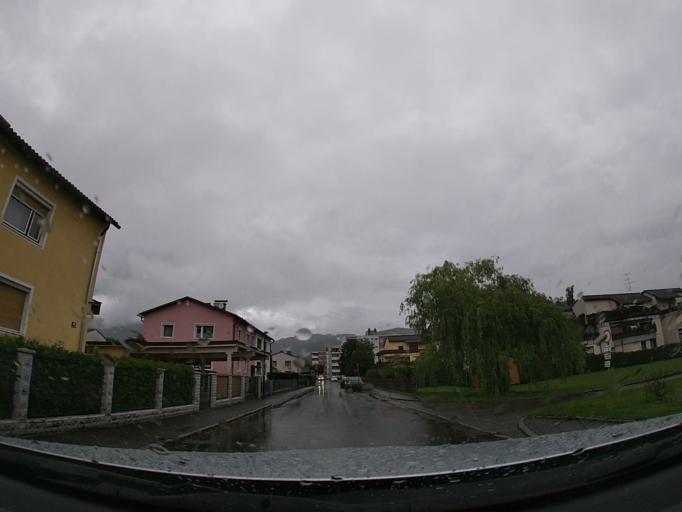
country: AT
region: Styria
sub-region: Politischer Bezirk Leoben
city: Trofaiach
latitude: 47.4230
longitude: 14.9918
